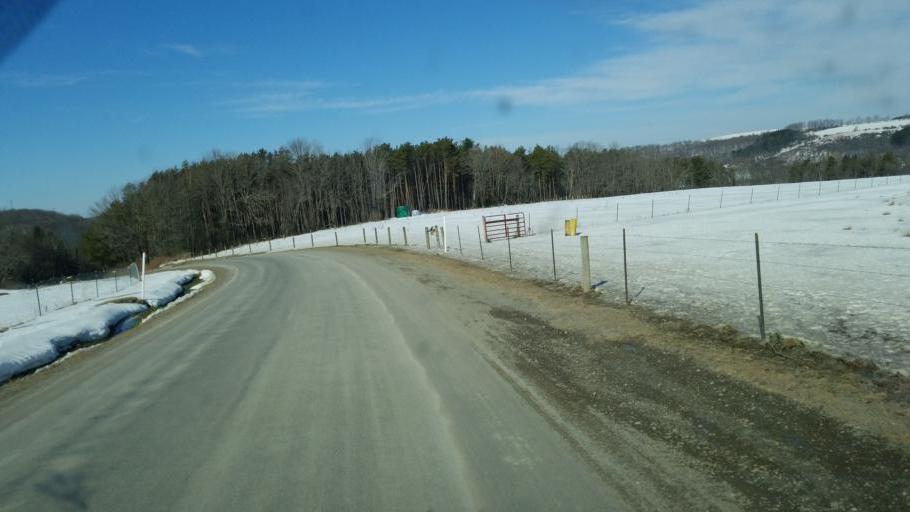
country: US
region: New York
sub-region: Allegany County
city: Andover
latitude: 42.1446
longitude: -77.7625
